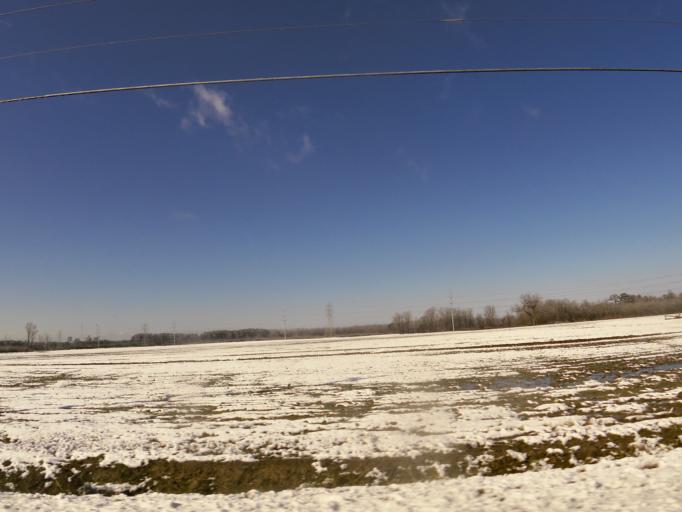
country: US
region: North Carolina
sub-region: Wilson County
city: Elm City
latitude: 35.7772
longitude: -77.8577
